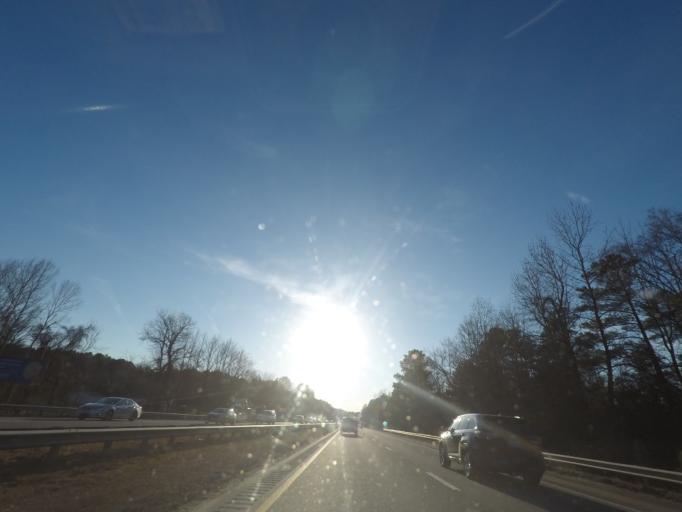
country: US
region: North Carolina
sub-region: Durham County
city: Gorman
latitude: 36.0436
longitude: -78.8193
